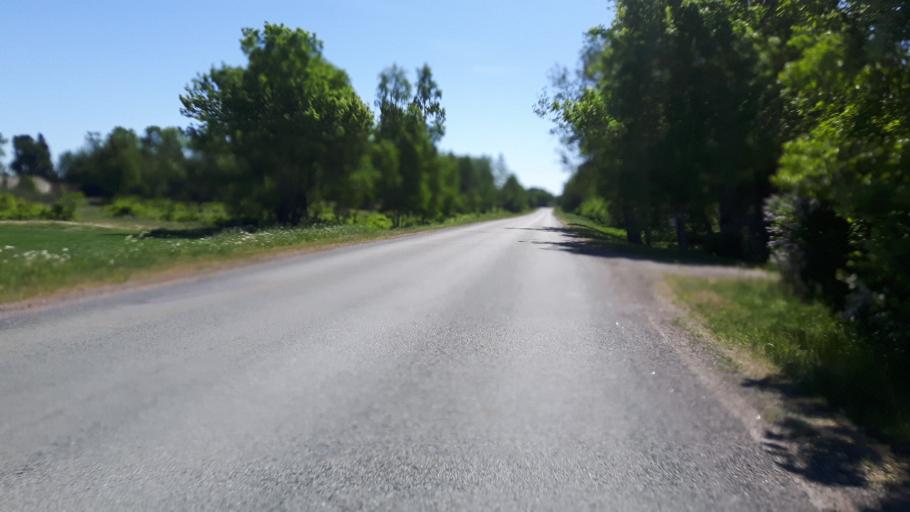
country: EE
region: Harju
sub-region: Kuusalu vald
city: Kuusalu
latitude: 59.4636
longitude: 25.4490
